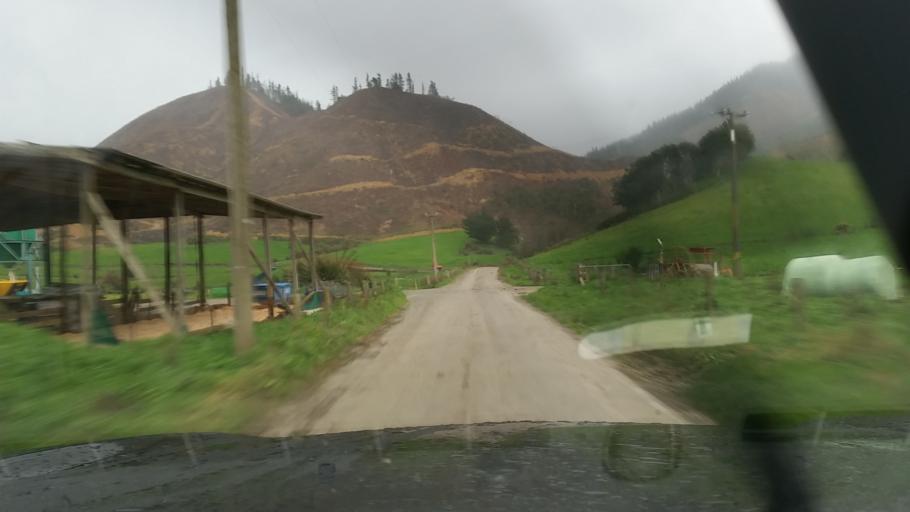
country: NZ
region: Marlborough
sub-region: Marlborough District
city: Picton
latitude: -41.3379
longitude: 173.9286
